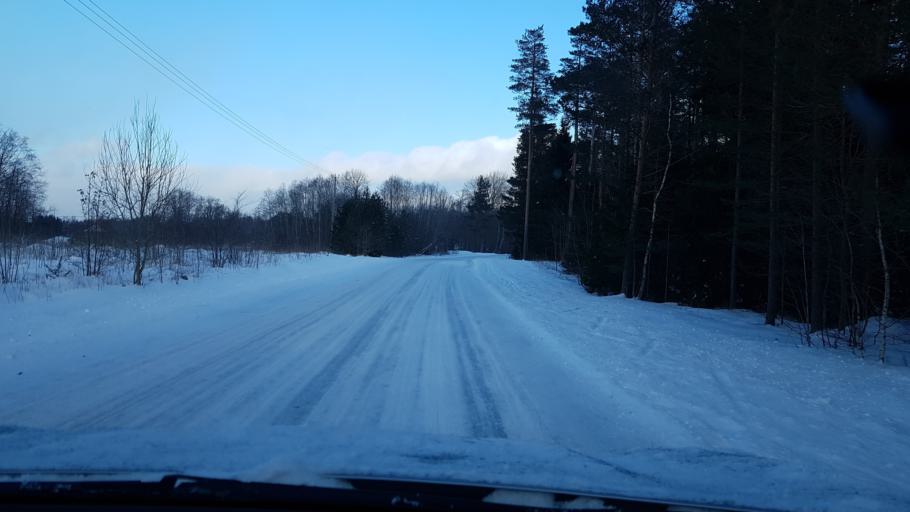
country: EE
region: Harju
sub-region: Nissi vald
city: Turba
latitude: 59.2199
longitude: 24.1403
